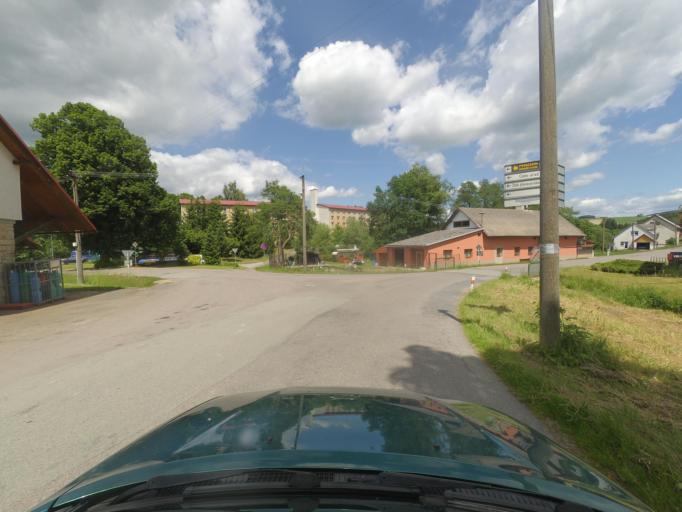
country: CZ
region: Pardubicky
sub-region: Okres Usti nad Orlici
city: Kunvald
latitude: 50.1097
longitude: 16.5391
